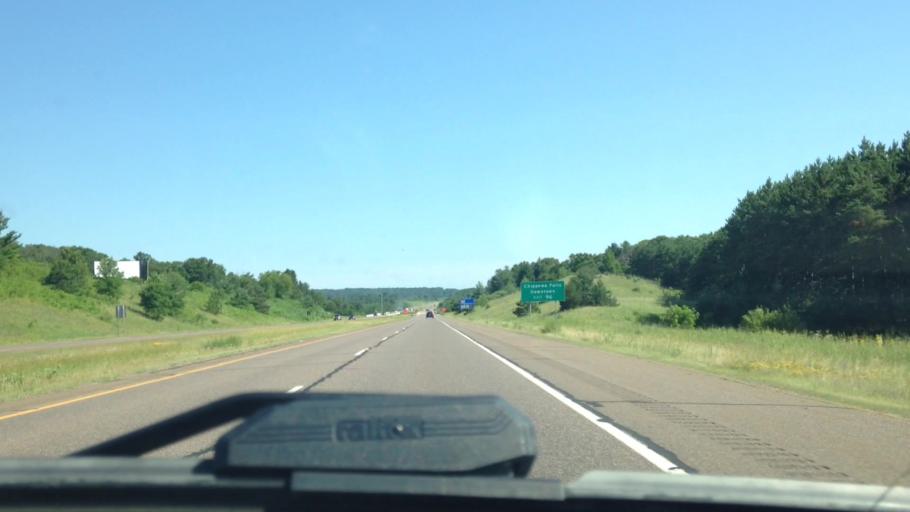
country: US
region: Wisconsin
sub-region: Chippewa County
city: Chippewa Falls
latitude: 44.9163
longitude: -91.4278
